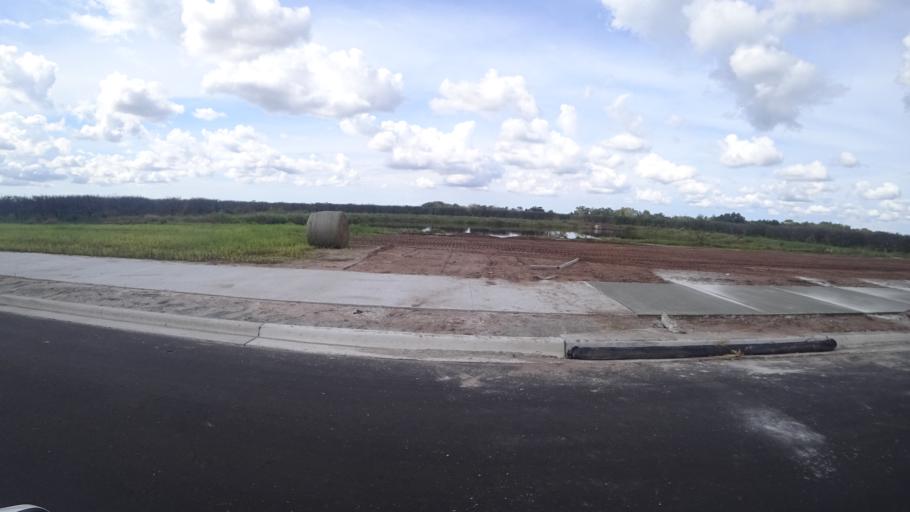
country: US
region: Florida
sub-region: Sarasota County
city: The Meadows
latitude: 27.4716
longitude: -82.3510
